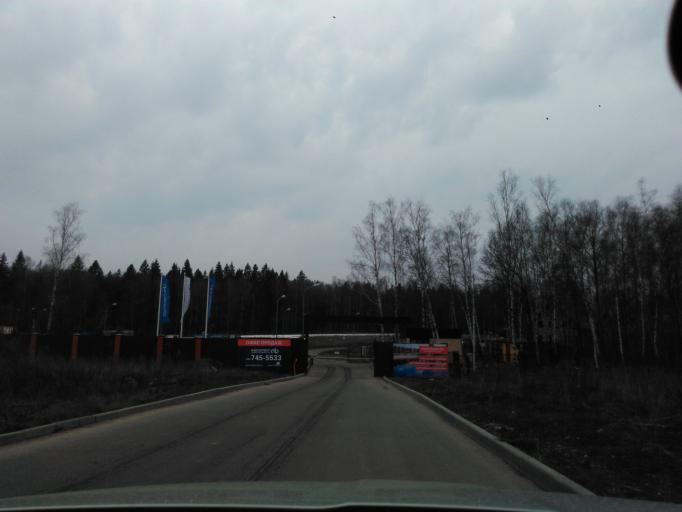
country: RU
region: Moskovskaya
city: Chashnikovo
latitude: 56.0355
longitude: 37.1509
